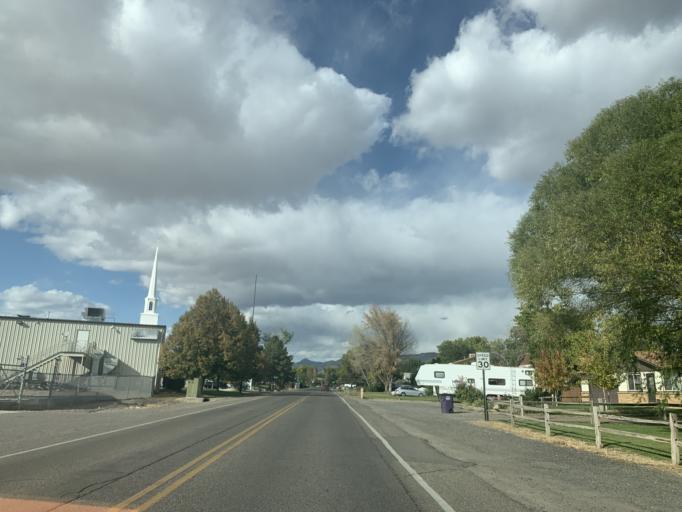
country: US
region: Colorado
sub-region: Mesa County
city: Fruitvale
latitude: 39.0822
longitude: -108.4785
